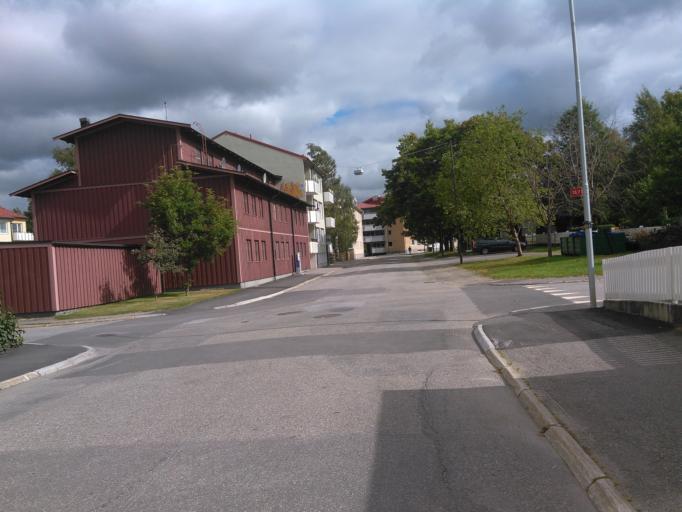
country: SE
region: Vaesterbotten
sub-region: Umea Kommun
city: Umea
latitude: 63.8288
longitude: 20.2473
